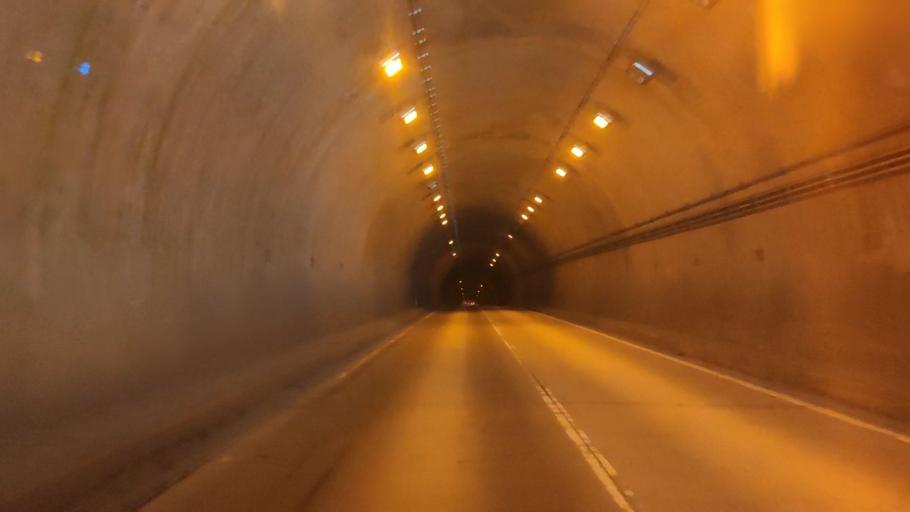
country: JP
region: Kumamoto
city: Hitoyoshi
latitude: 32.4169
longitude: 130.8452
